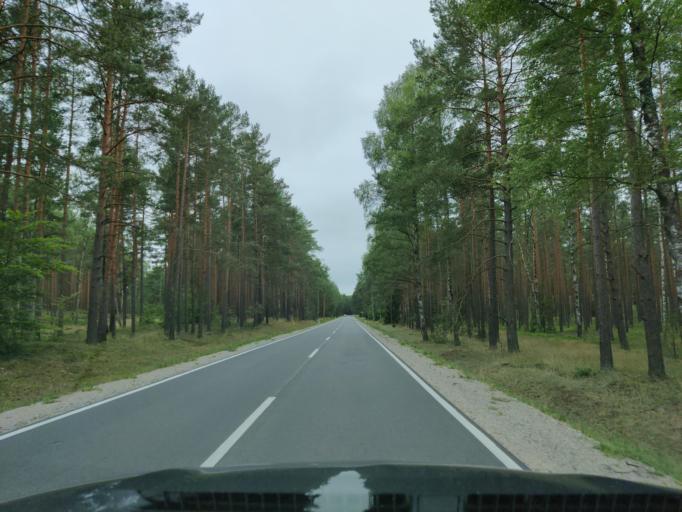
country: PL
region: Masovian Voivodeship
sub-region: Powiat ostrolecki
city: Czarnia
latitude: 53.3401
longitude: 21.2319
